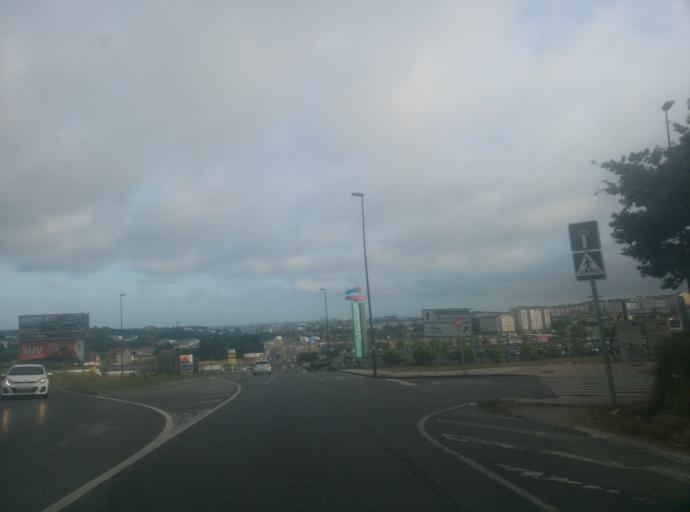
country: ES
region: Galicia
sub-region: Provincia de Lugo
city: Lugo
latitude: 43.0399
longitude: -7.5677
